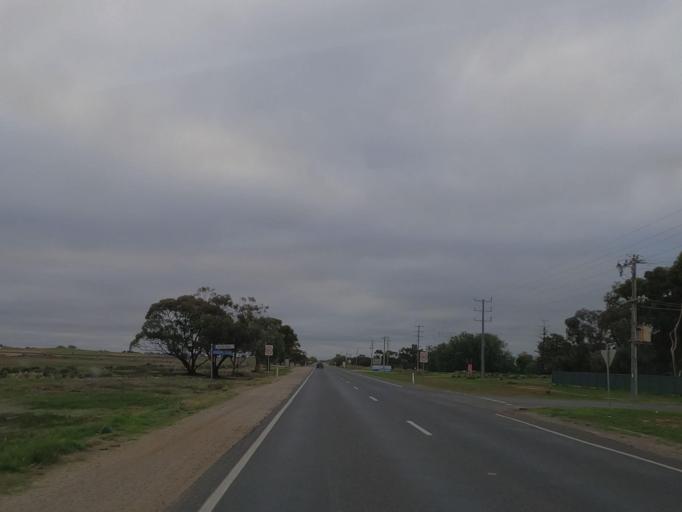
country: AU
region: Victoria
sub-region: Swan Hill
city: Swan Hill
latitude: -35.4526
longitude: 143.6261
